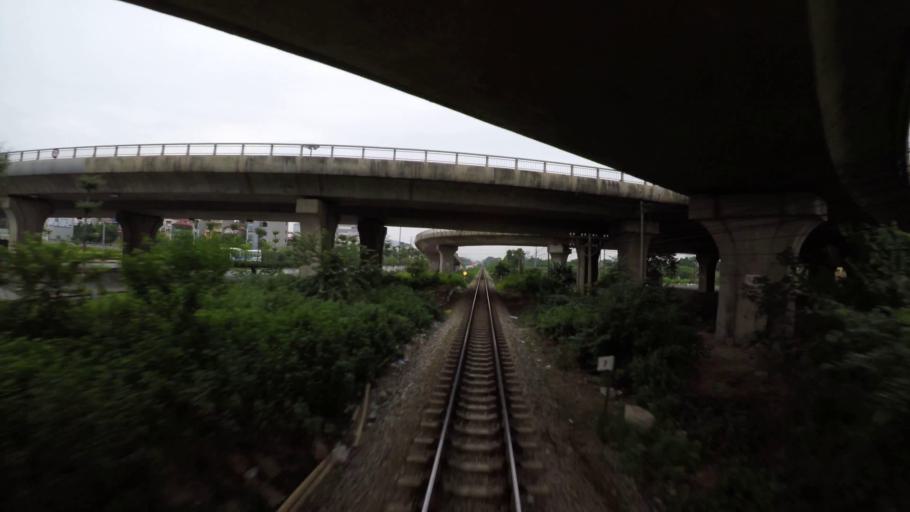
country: VN
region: Ha Noi
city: Trau Quy
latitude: 21.0070
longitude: 105.9575
